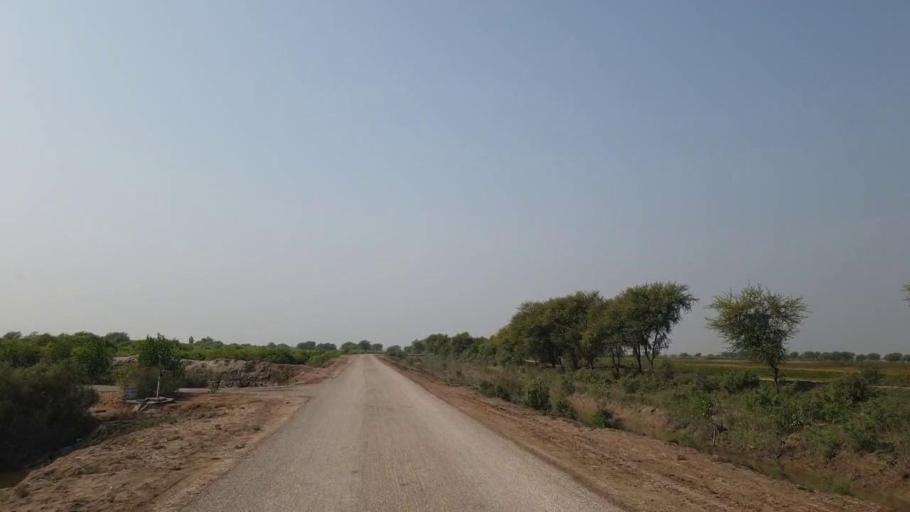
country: PK
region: Sindh
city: Kario
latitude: 24.9469
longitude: 68.5315
